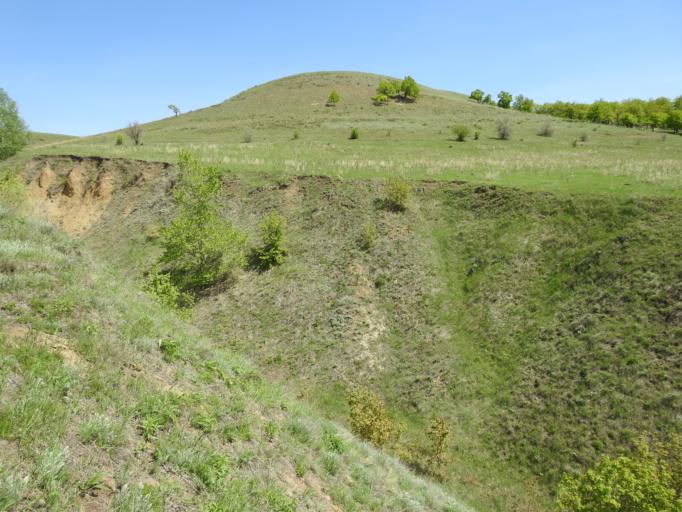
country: RU
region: Saratov
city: Krasnyy Oktyabr'
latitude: 51.5954
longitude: 45.7199
